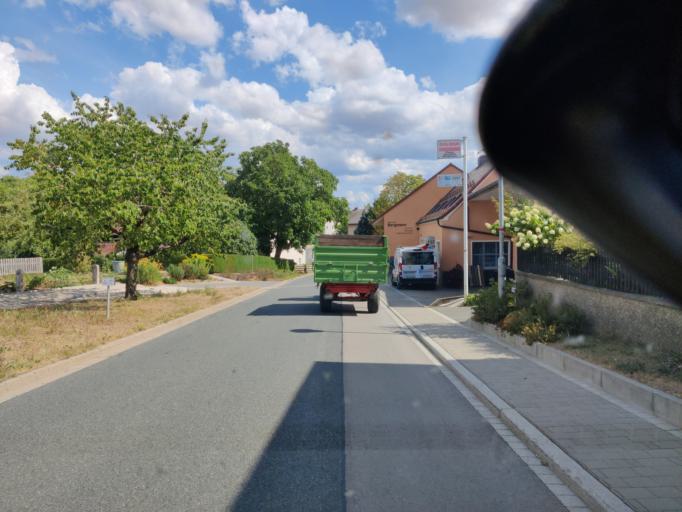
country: DE
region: Bavaria
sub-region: Regierungsbezirk Mittelfranken
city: Thalmassing
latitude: 49.0699
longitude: 11.2222
